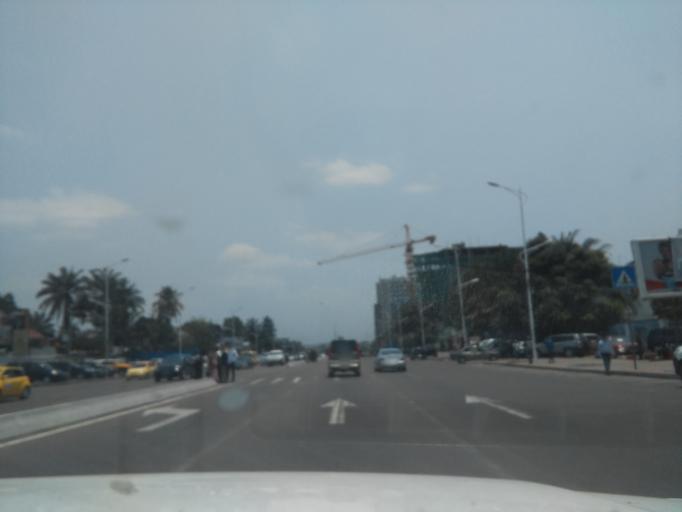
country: CD
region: Kinshasa
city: Kinshasa
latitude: -4.3146
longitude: 15.2826
